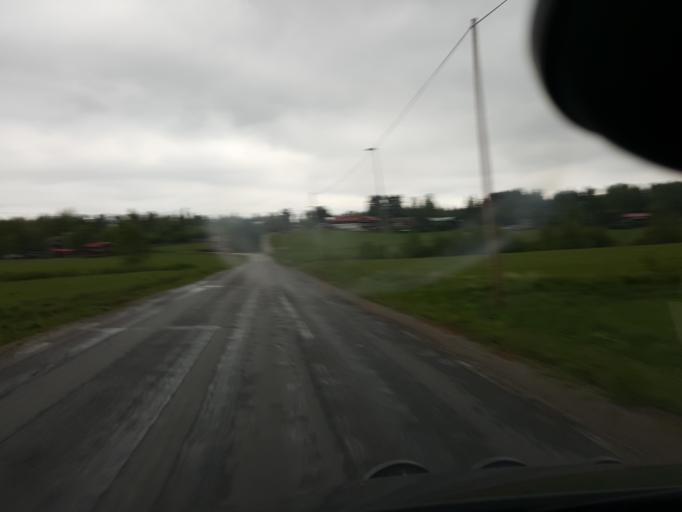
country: SE
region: Gaevleborg
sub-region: Ljusdals Kommun
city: Jaervsoe
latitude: 61.7117
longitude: 16.1967
